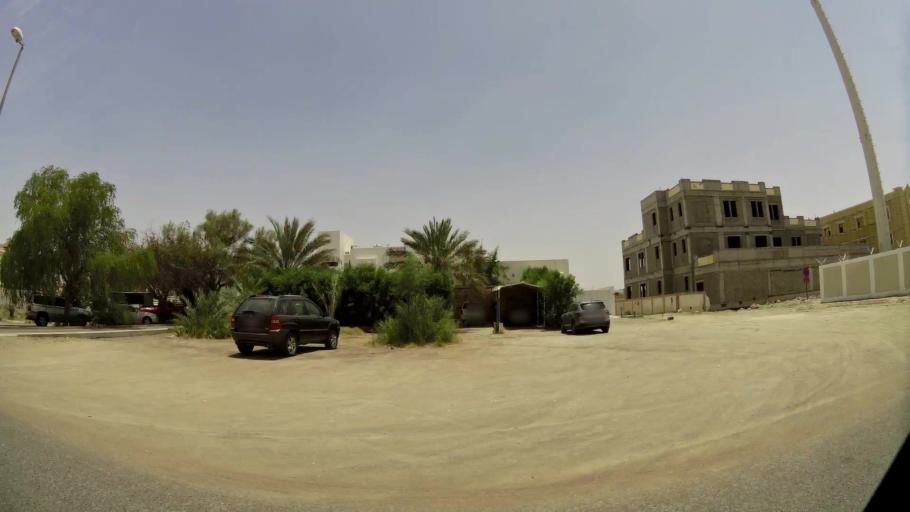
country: AE
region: Abu Dhabi
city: Al Ain
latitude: 24.2106
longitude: 55.7285
